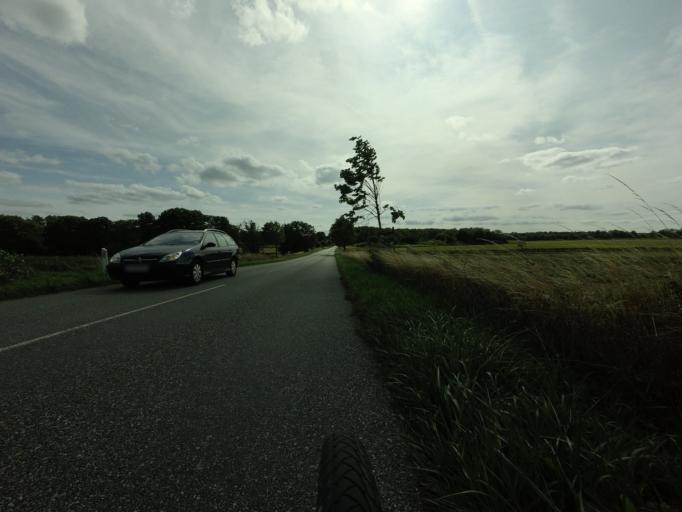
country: DK
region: Zealand
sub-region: Faxe Kommune
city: Fakse Ladeplads
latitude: 55.2418
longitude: 12.2172
